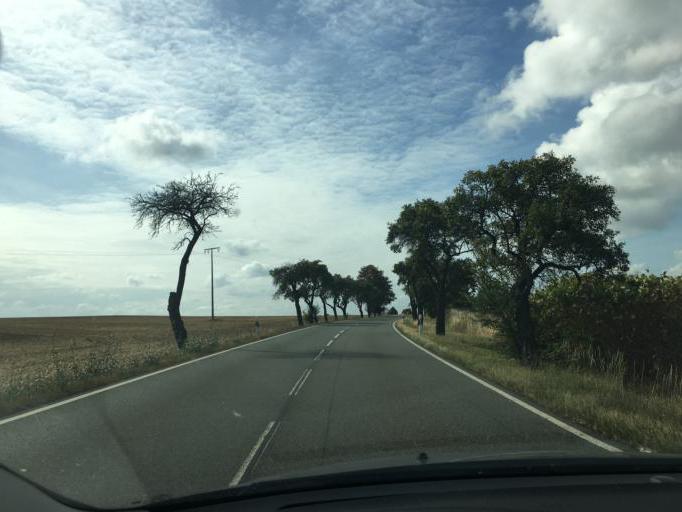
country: DE
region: Thuringia
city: Oettersdorf
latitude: 50.5997
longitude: 11.8246
